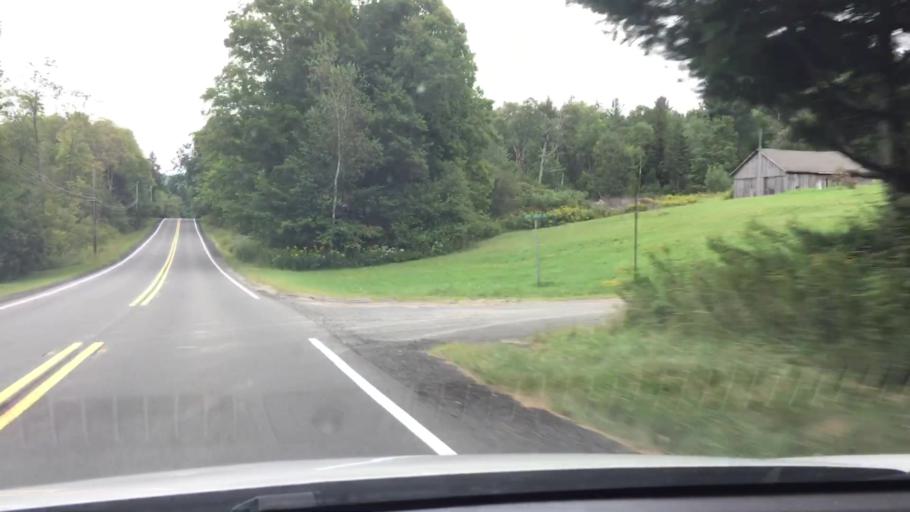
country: US
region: Massachusetts
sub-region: Berkshire County
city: Becket
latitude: 42.3445
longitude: -73.0923
